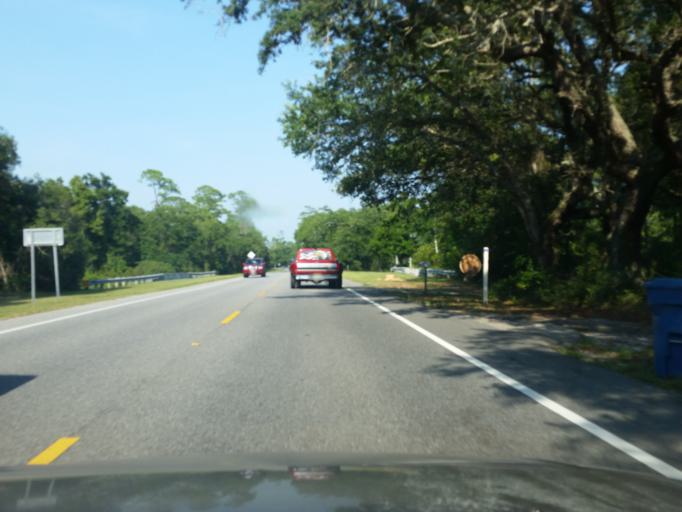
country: US
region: Alabama
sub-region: Baldwin County
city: Gulf Shores
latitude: 30.2479
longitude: -87.7716
